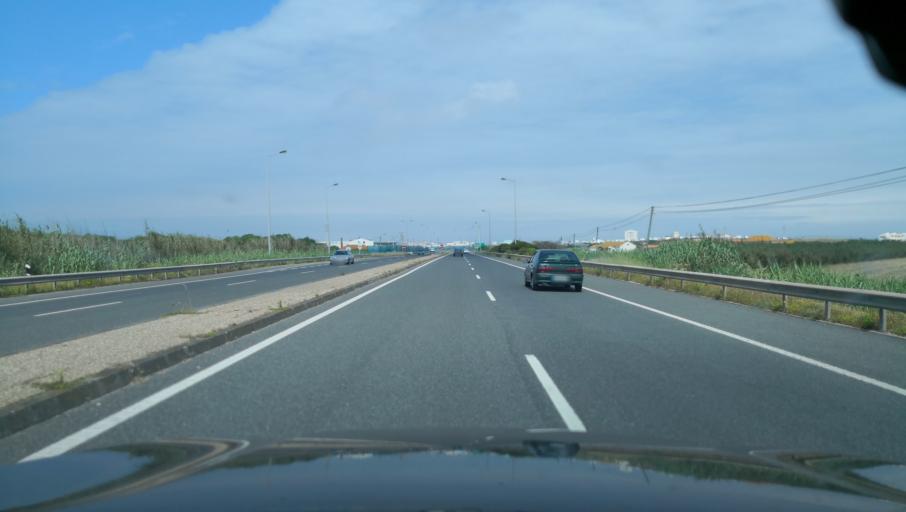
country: PT
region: Leiria
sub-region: Peniche
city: Atouguia da Baleia
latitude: 39.3489
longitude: -9.3514
